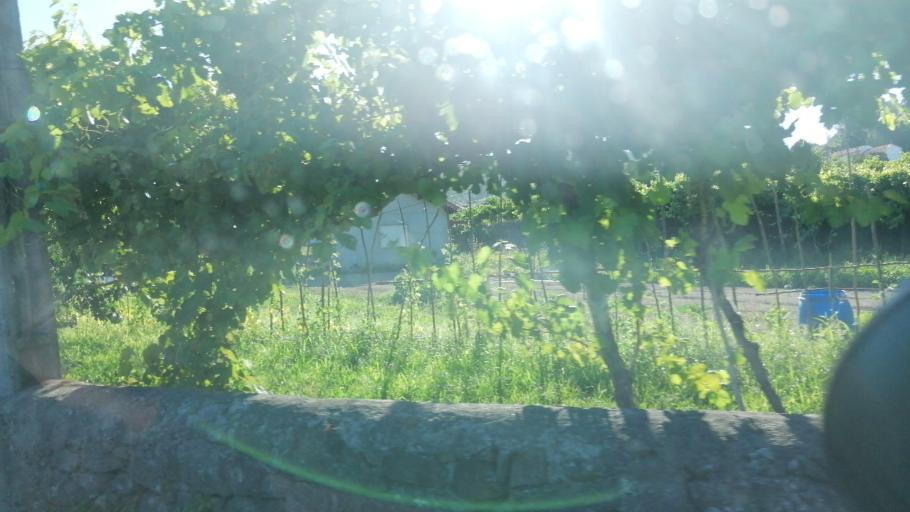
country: PT
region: Porto
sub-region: Santo Tirso
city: Sao Miguel do Couto
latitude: 41.2893
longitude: -8.4712
